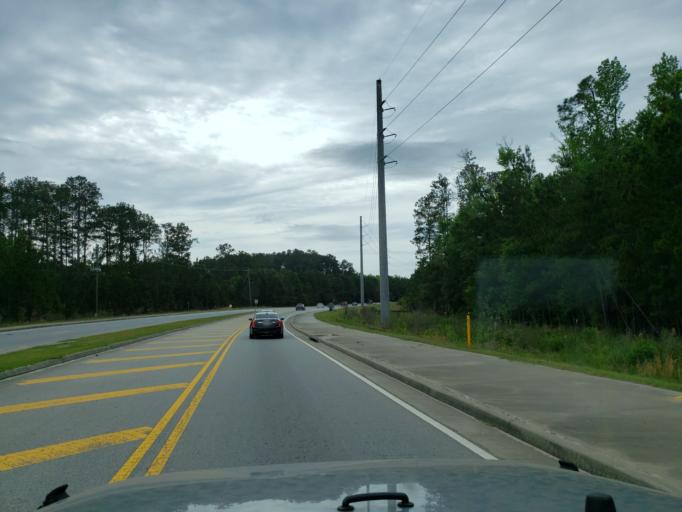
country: US
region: Georgia
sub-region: Chatham County
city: Pooler
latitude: 32.1631
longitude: -81.2329
